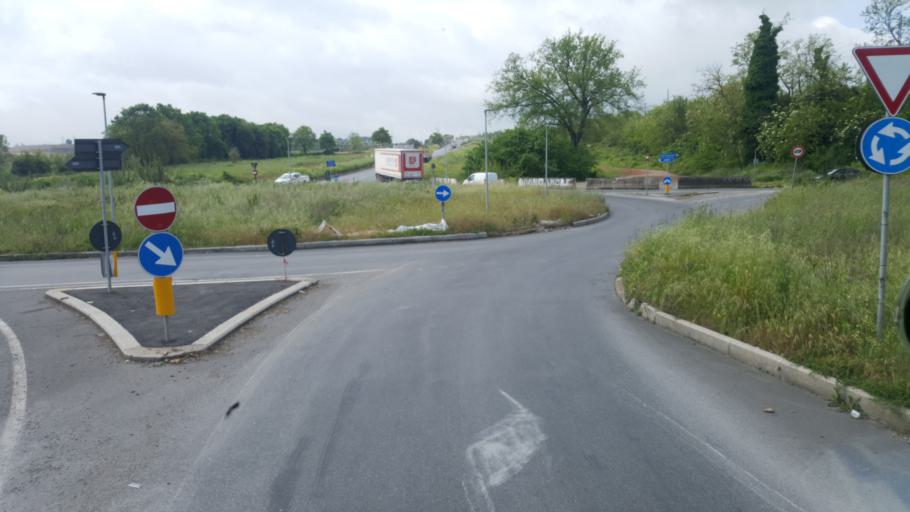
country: IT
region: Latium
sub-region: Citta metropolitana di Roma Capitale
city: Borgo Lotti
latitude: 41.7574
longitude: 12.5600
